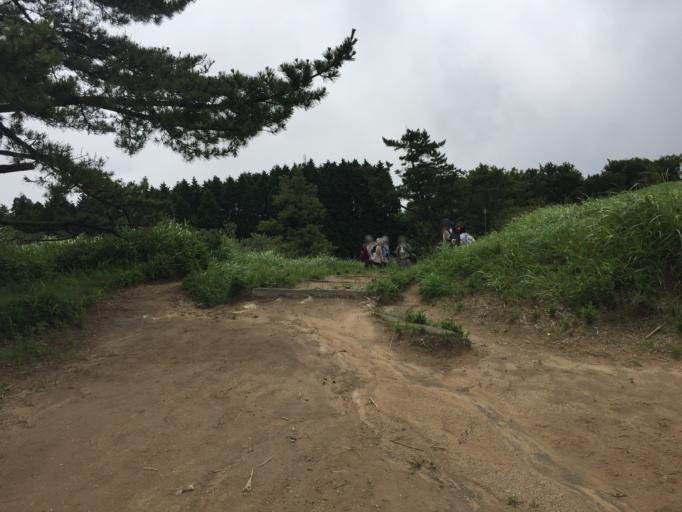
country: JP
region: Nara
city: Gose
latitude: 34.4561
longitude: 135.6825
